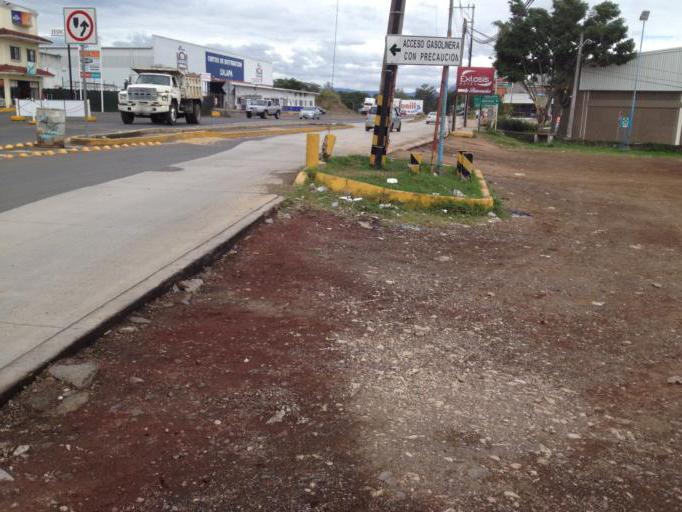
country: MX
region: Veracruz
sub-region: Emiliano Zapata
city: Las Trancas
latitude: 19.5007
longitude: -96.8606
